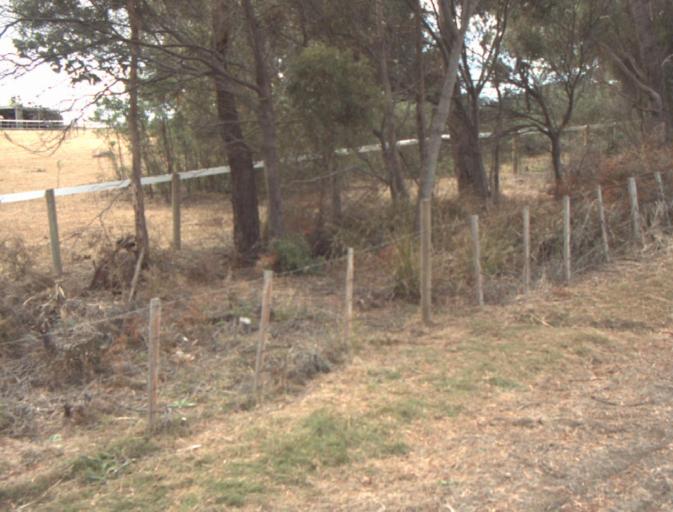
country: AU
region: Tasmania
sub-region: Launceston
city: Mayfield
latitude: -41.2806
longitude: 147.0432
